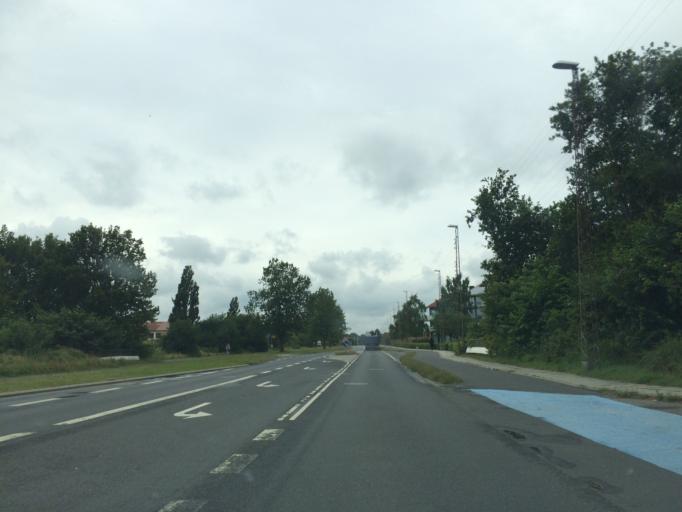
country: DK
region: Central Jutland
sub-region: Silkeborg Kommune
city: Silkeborg
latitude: 56.1832
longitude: 9.5701
